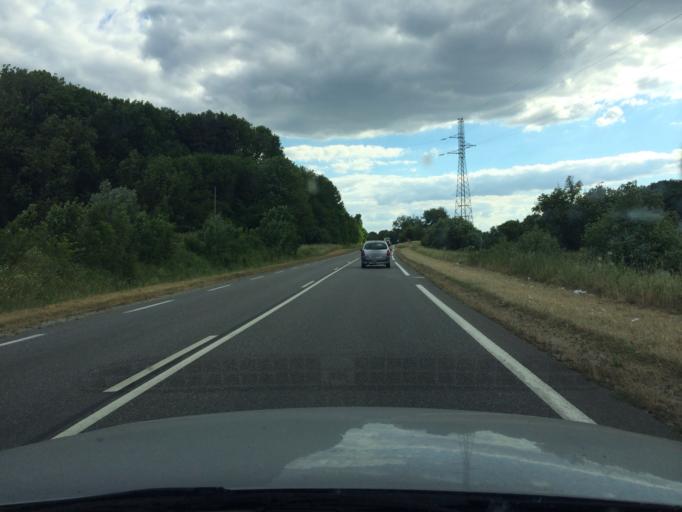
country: FR
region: Lorraine
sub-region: Departement de la Moselle
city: Lorquin
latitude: 48.6216
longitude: 6.8803
